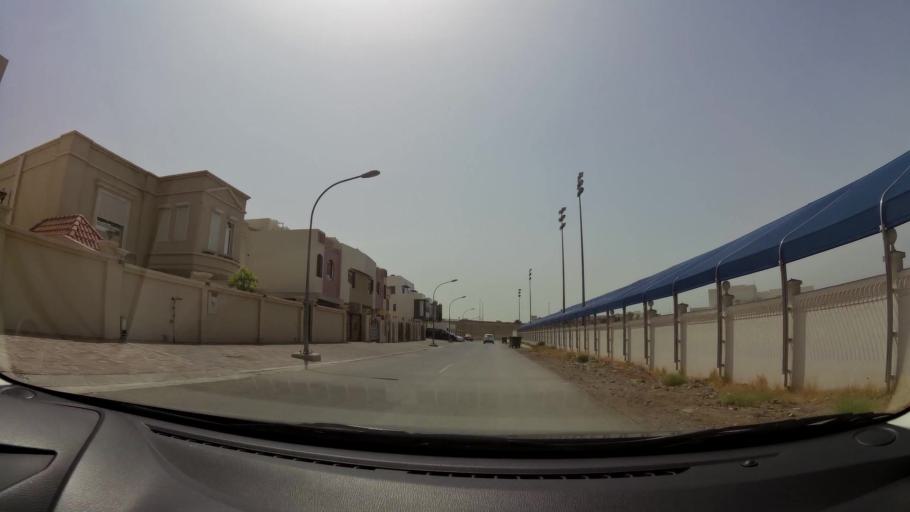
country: OM
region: Muhafazat Masqat
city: Bawshar
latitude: 23.5678
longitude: 58.3821
